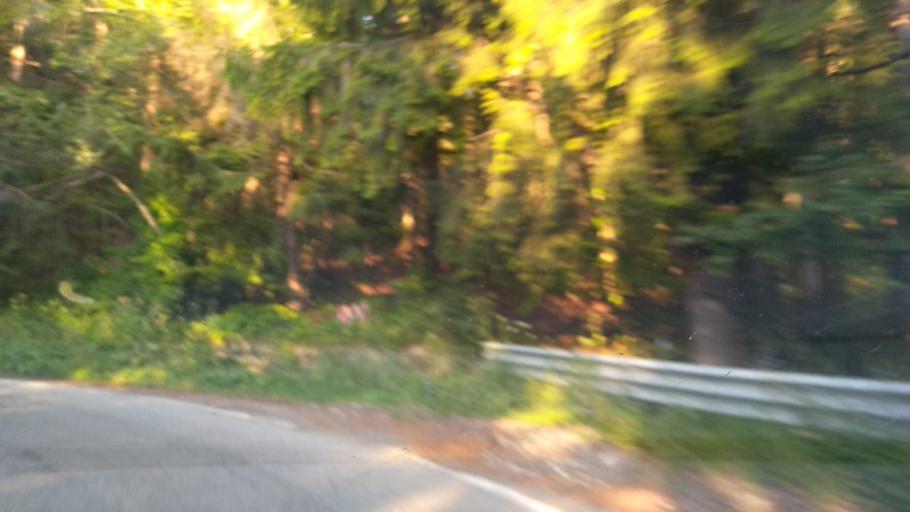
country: RO
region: Prahova
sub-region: Oras Sinaia
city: Sinaia
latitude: 45.3269
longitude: 25.5172
